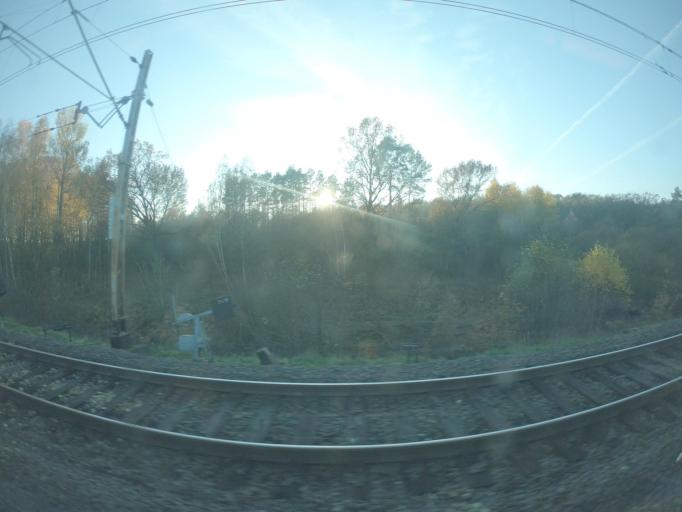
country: PL
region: Lubusz
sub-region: Powiat sulecinski
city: Torzym
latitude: 52.2507
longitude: 14.9574
